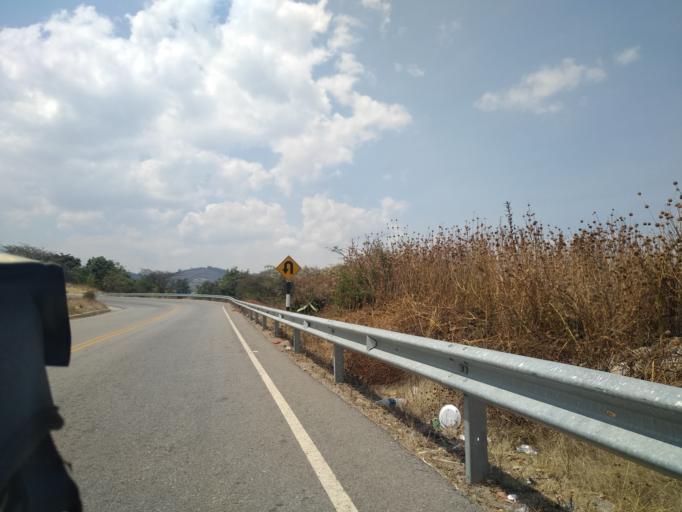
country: PE
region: Cajamarca
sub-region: Provincia de Cajabamba
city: Cauday
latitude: -7.6137
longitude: -78.0861
